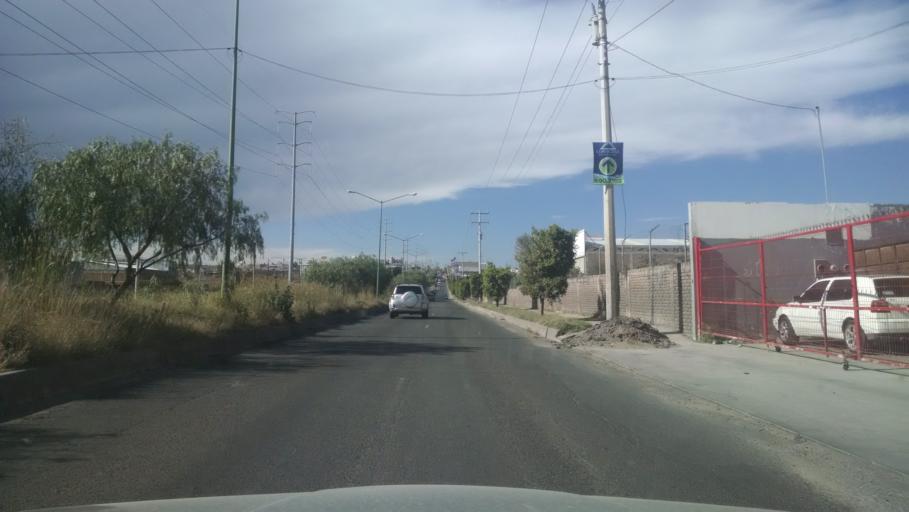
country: MX
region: Guanajuato
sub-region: Leon
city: La Ermita
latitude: 21.1470
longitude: -101.7275
